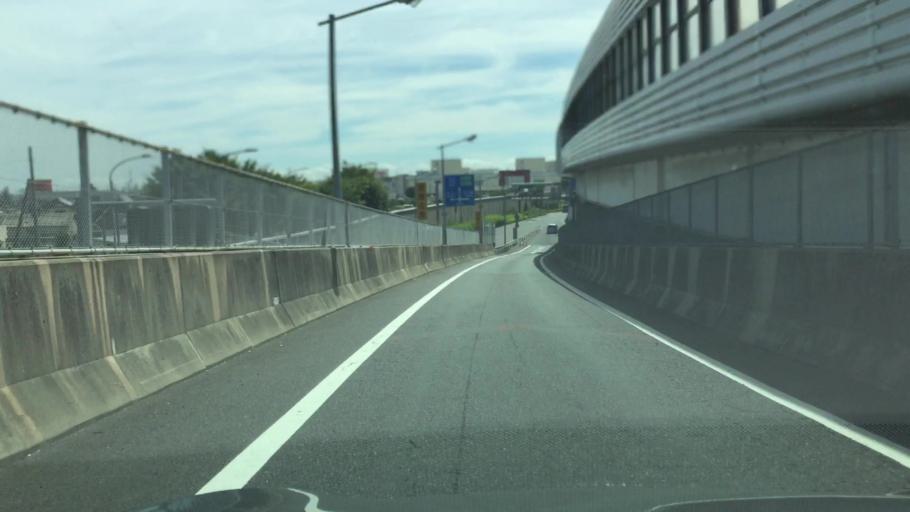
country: JP
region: Saitama
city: Yashio-shi
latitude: 35.8443
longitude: 139.8484
